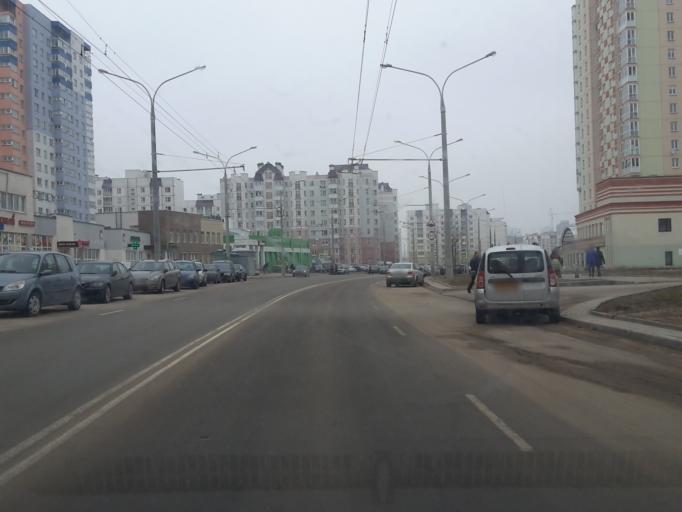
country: BY
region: Minsk
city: Novoye Medvezhino
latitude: 53.8898
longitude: 27.4214
